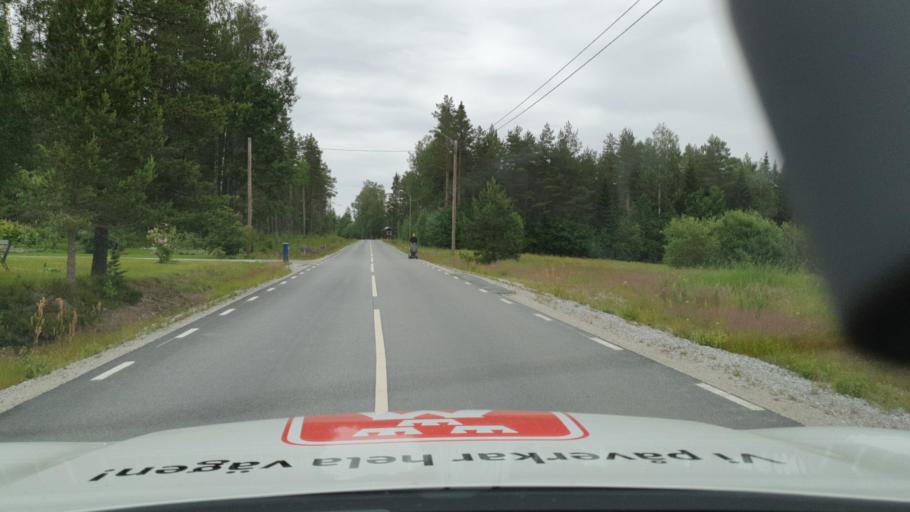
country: SE
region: Vaesterbotten
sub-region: Nordmalings Kommun
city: Nordmaling
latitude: 63.5176
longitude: 19.3572
